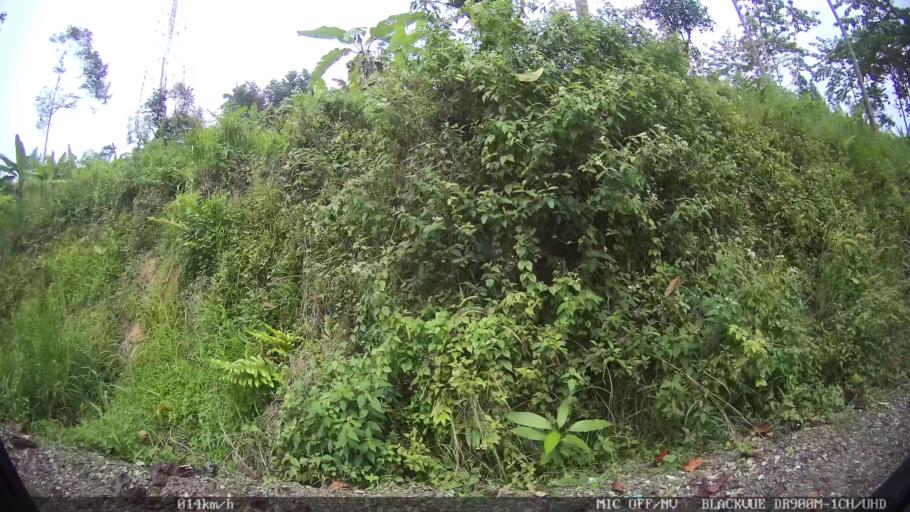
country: ID
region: Lampung
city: Panjang
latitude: -5.4298
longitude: 105.3092
